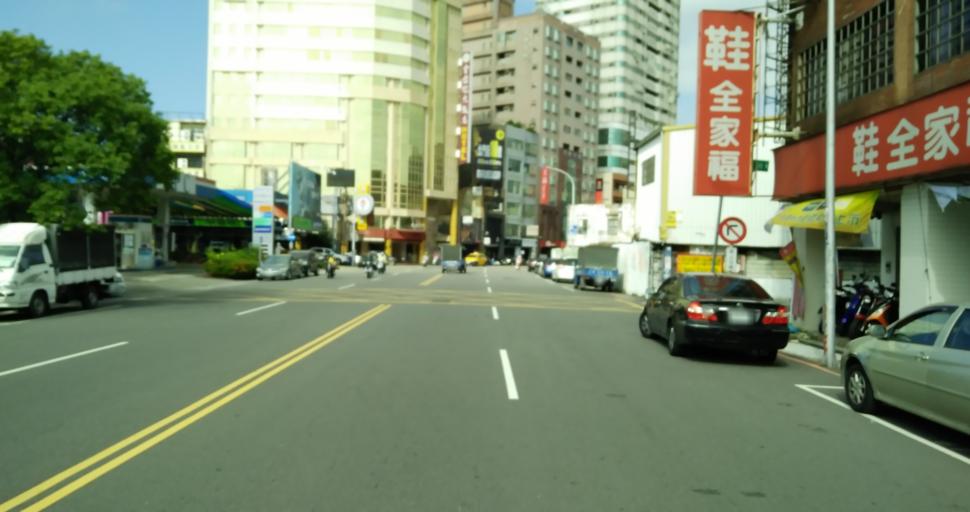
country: TW
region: Taiwan
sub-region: Hsinchu
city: Hsinchu
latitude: 24.8047
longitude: 120.9610
